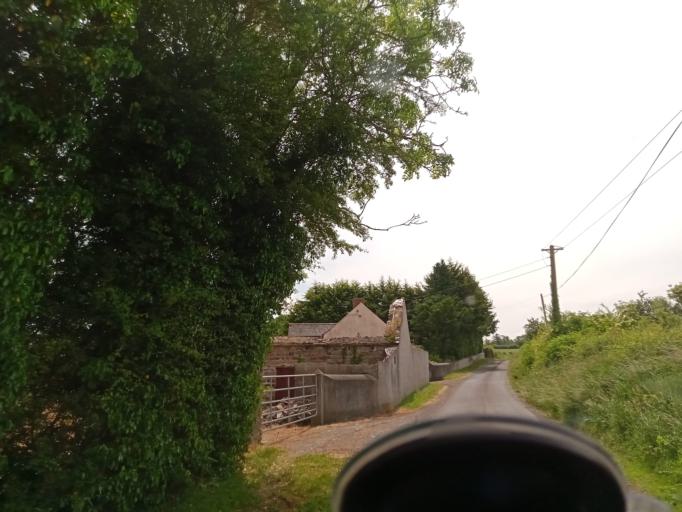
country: IE
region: Leinster
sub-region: Kilkenny
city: Thomastown
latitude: 52.5626
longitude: -7.1026
